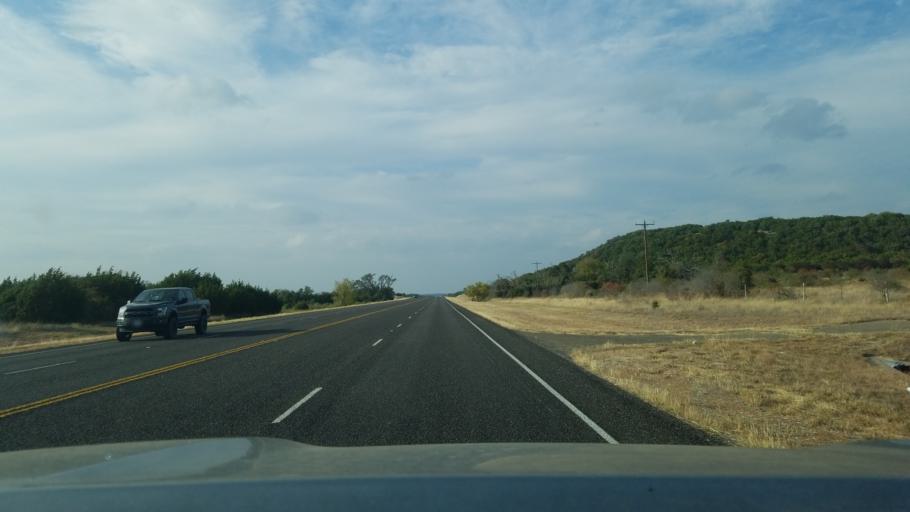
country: US
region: Texas
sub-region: Mills County
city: Goldthwaite
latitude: 31.2659
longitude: -98.4421
